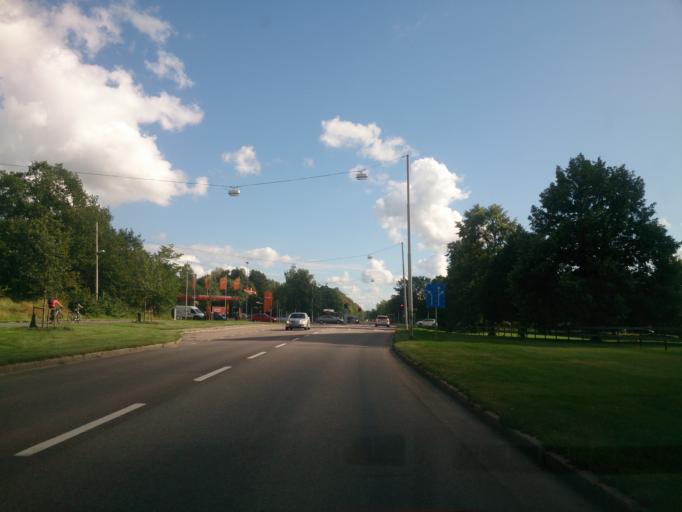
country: SE
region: OEstergoetland
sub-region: Linkopings Kommun
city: Linkoping
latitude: 58.3942
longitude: 15.6444
